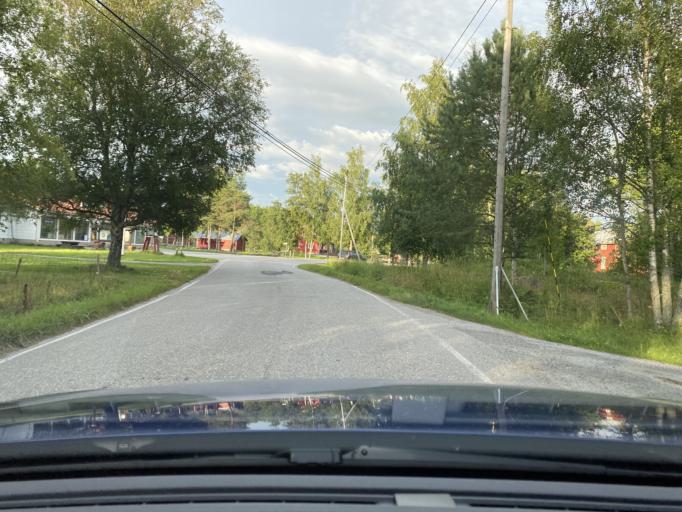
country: FI
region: Ostrobothnia
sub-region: Vaasa
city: Korsnaes
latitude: 62.9704
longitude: 21.1869
